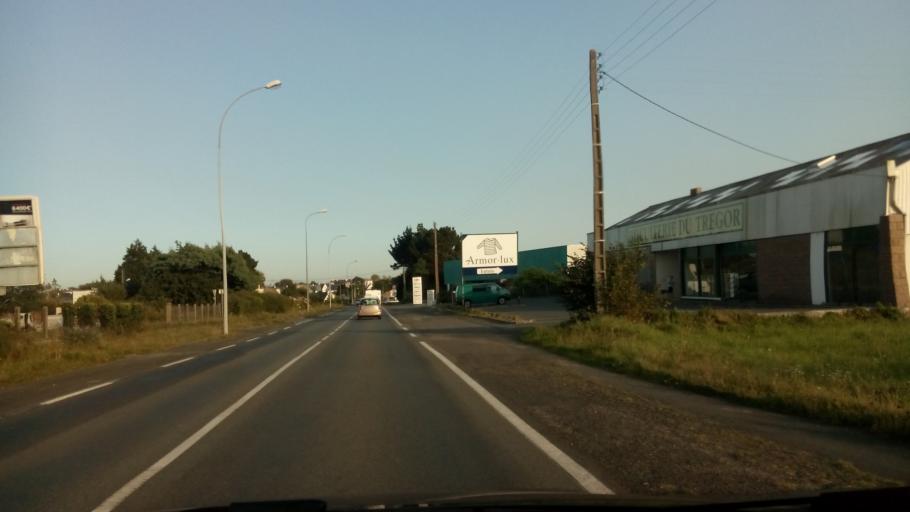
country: FR
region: Brittany
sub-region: Departement des Cotes-d'Armor
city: Lannion
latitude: 48.7476
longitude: -3.4828
